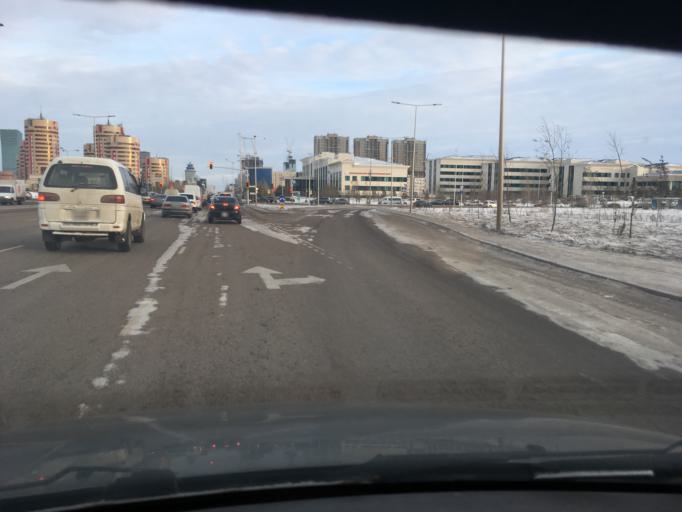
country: KZ
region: Astana Qalasy
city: Astana
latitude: 51.1272
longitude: 71.4027
